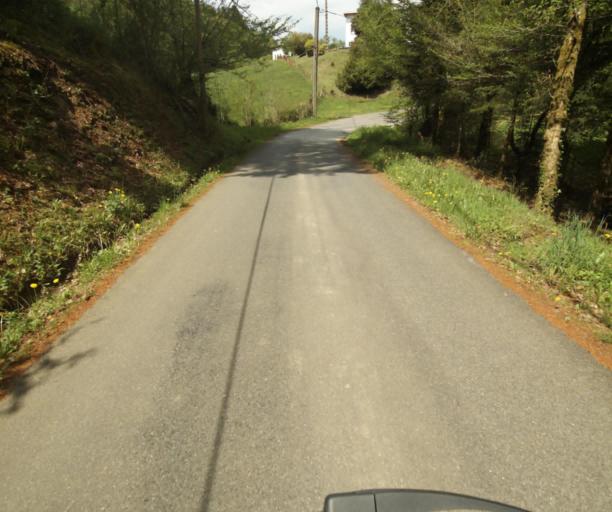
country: FR
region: Limousin
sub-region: Departement de la Correze
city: Tulle
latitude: 45.2783
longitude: 1.7554
